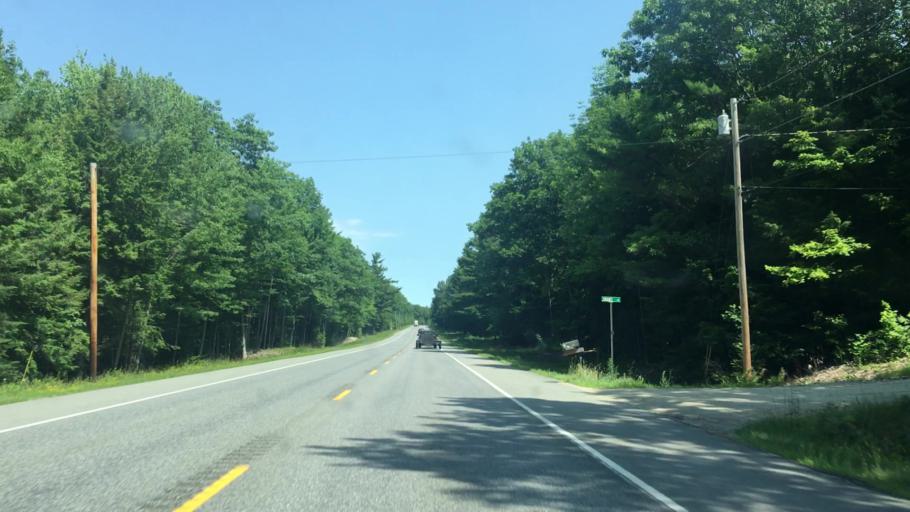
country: US
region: Maine
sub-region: Kennebec County
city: Monmouth
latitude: 44.2400
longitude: -70.0685
